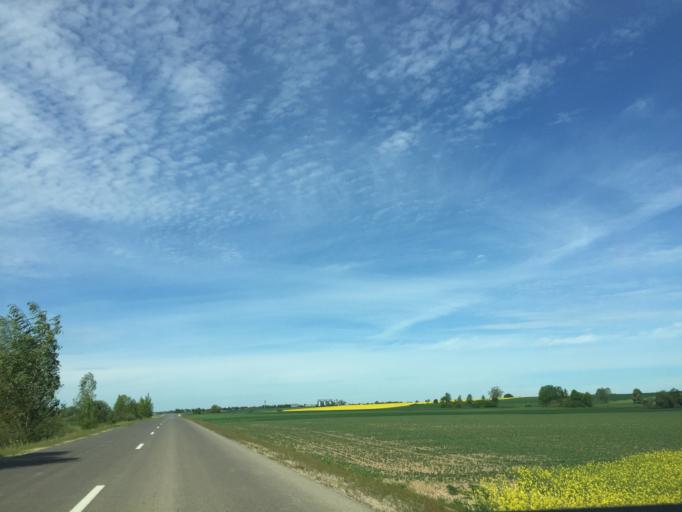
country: LT
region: Panevezys
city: Pasvalys
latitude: 56.1127
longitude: 24.2104
